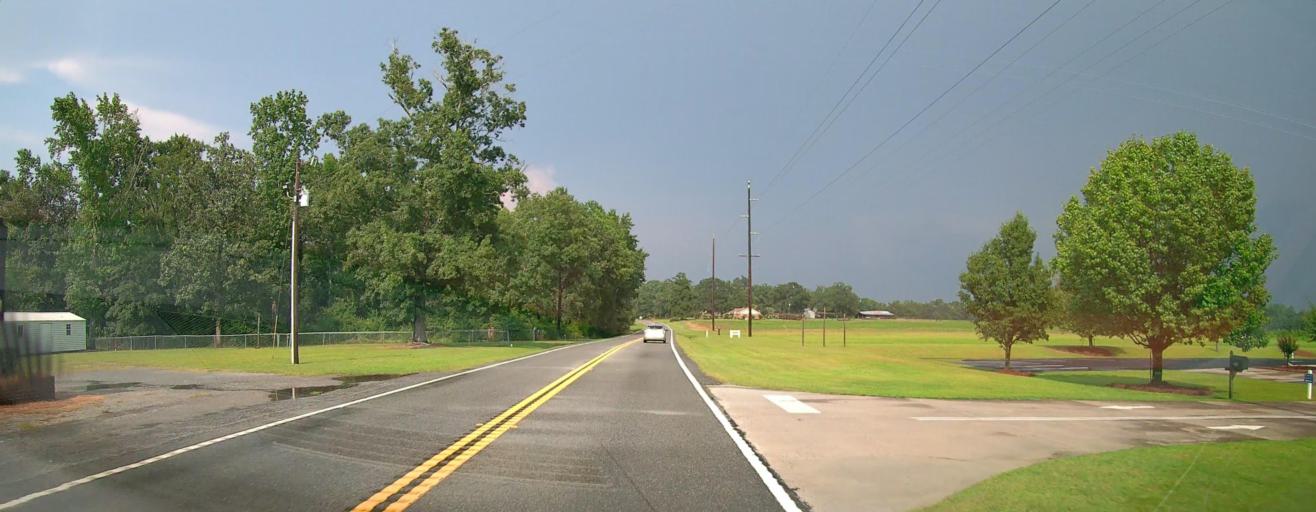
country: US
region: Georgia
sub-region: Twiggs County
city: Jeffersonville
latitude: 32.6004
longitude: -83.3069
